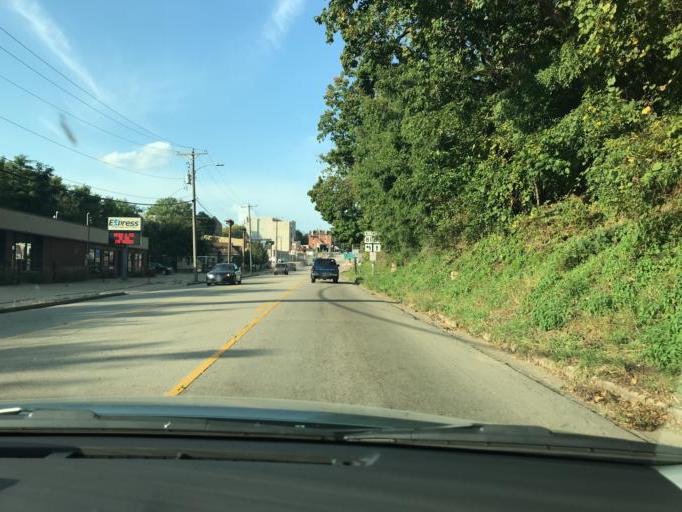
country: US
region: Wisconsin
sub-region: Grant County
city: Platteville
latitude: 42.7308
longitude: -90.4758
